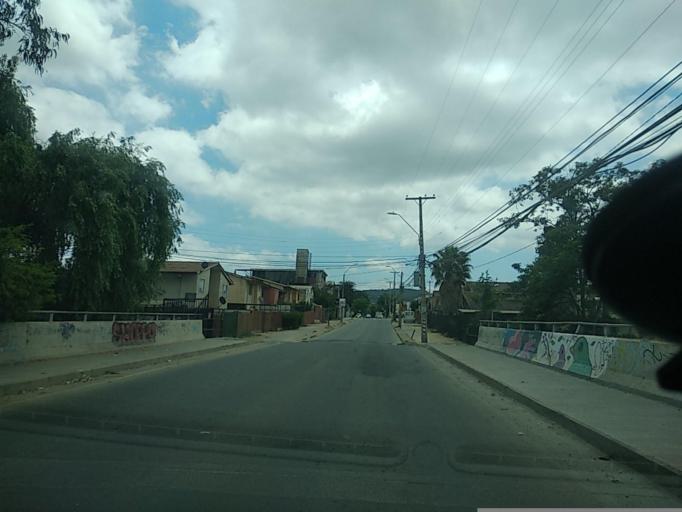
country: CL
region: Valparaiso
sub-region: Provincia de Marga Marga
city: Villa Alemana
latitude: -33.0404
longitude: -71.4054
